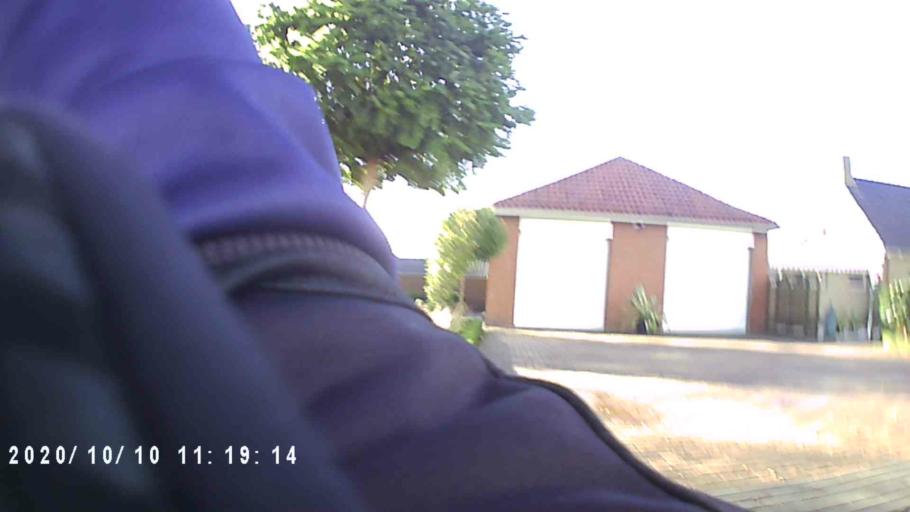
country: NL
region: Friesland
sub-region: Gemeente Smallingerland
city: Drachtstercompagnie
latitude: 53.0947
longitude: 6.1927
